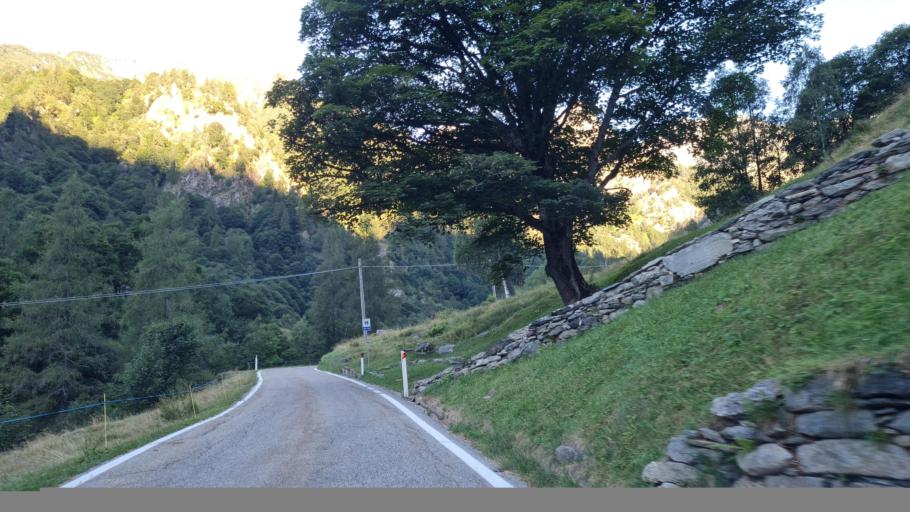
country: IT
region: Piedmont
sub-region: Provincia di Vercelli
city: Rima
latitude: 45.8802
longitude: 8.0092
